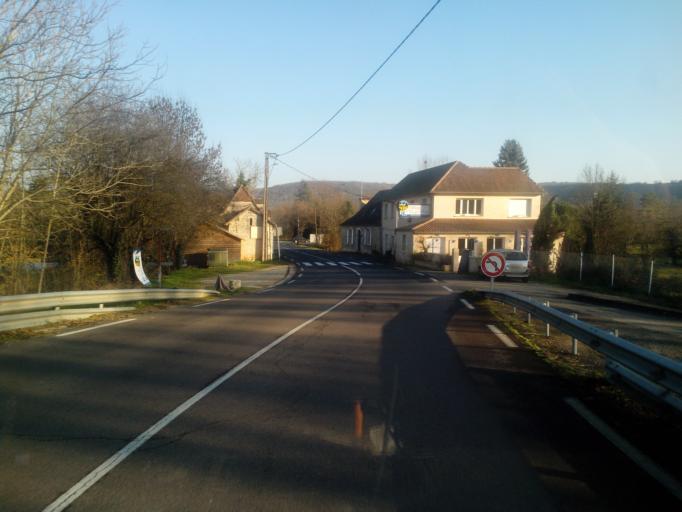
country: FR
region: Midi-Pyrenees
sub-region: Departement du Lot
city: Vayrac
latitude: 44.9083
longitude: 1.6290
